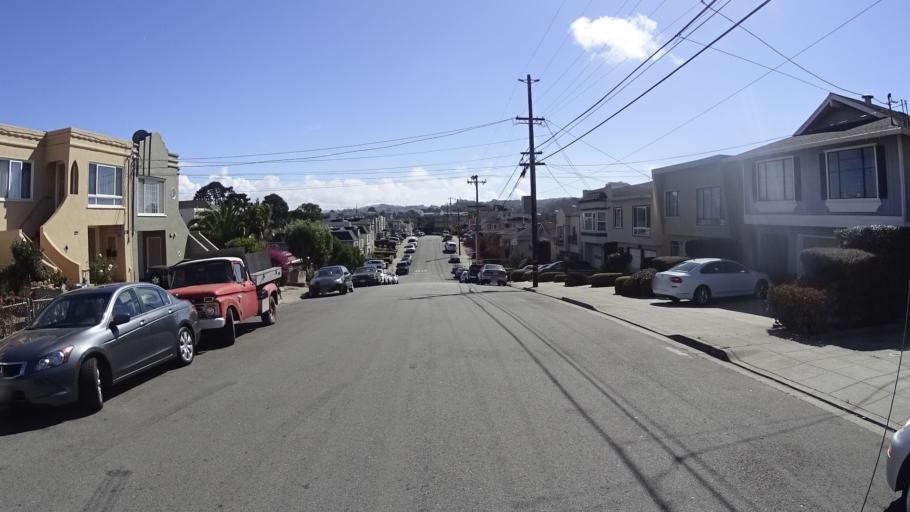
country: US
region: California
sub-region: San Mateo County
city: Broadmoor
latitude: 37.6922
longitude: -122.4690
